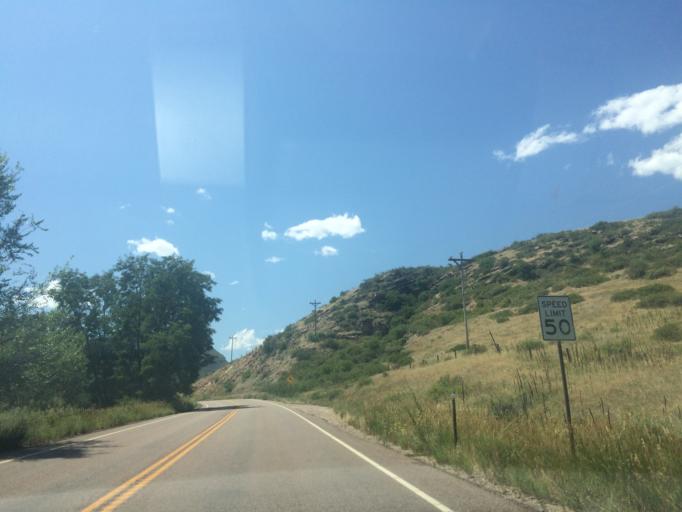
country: US
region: Colorado
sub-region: Boulder County
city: Lyons
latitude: 40.2174
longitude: -105.2745
